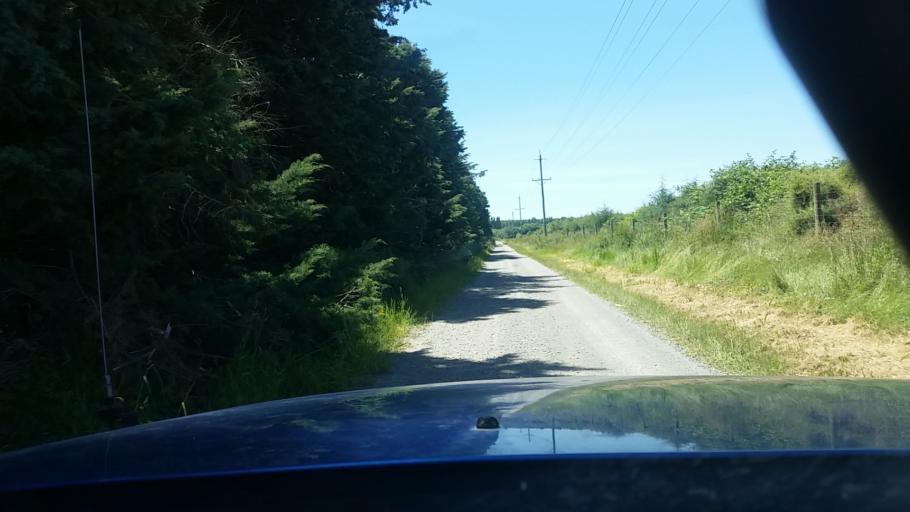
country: NZ
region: Canterbury
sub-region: Ashburton District
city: Tinwald
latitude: -43.9470
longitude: 171.7676
